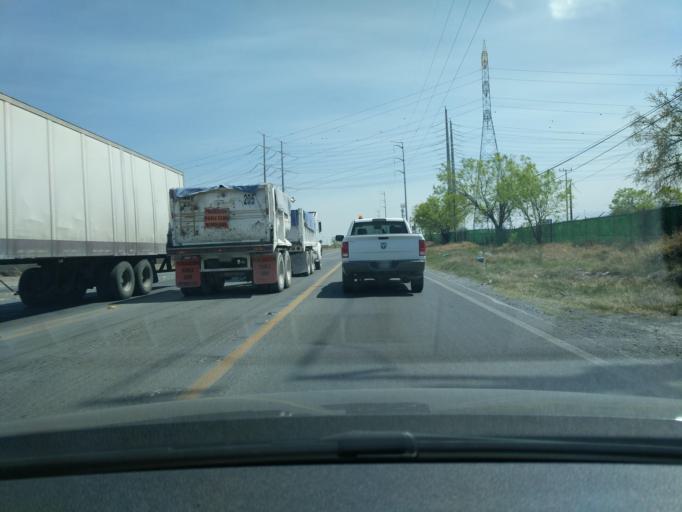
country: MX
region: Nuevo Leon
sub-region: El Carmen
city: Buena Vista
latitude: 25.8991
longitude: -100.3538
